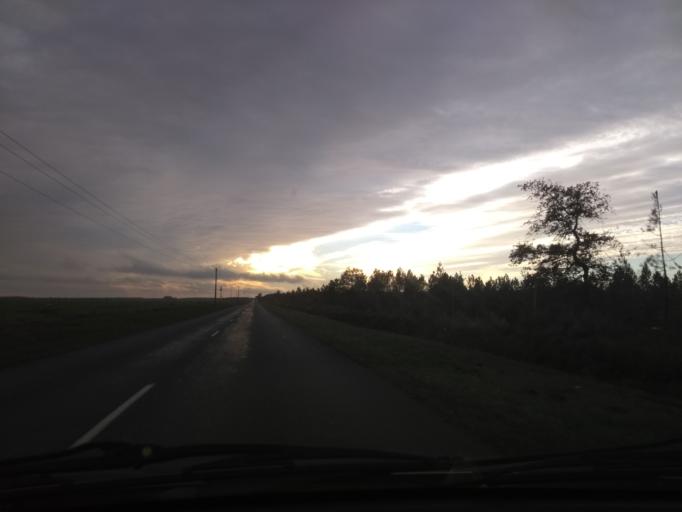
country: FR
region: Aquitaine
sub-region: Departement de la Gironde
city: Saucats
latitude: 44.6297
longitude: -0.6583
